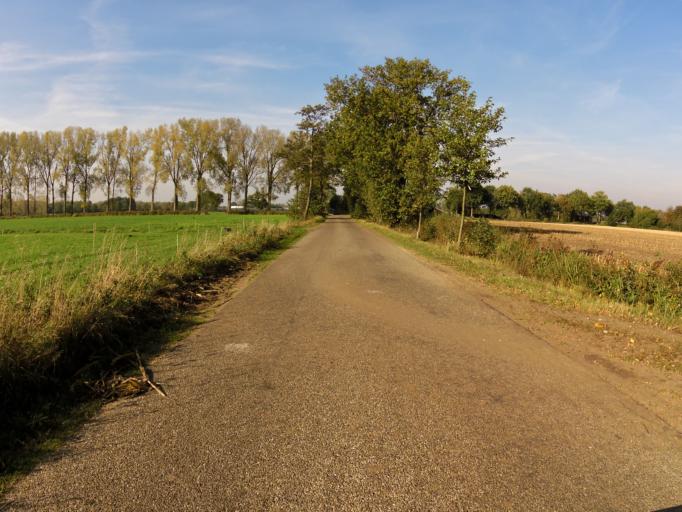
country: NL
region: North Brabant
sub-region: Gemeente Laarbeek
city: Aarle-Rixtel
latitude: 51.5359
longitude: 5.6793
